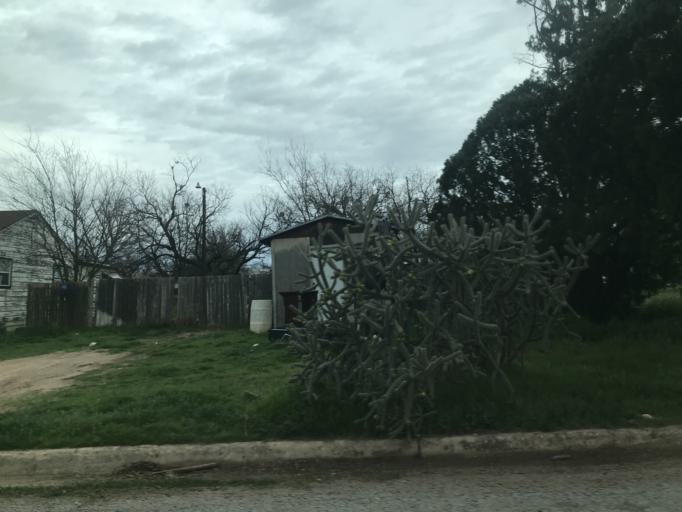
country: US
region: Texas
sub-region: Taylor County
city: Abilene
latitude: 32.4665
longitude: -99.7453
